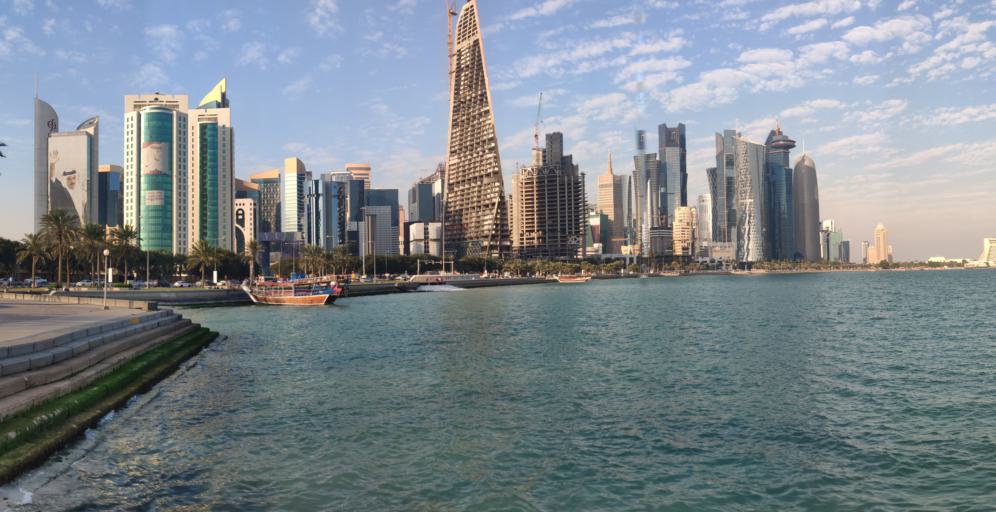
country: QA
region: Baladiyat ad Dawhah
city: Doha
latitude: 25.3091
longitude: 51.5199
